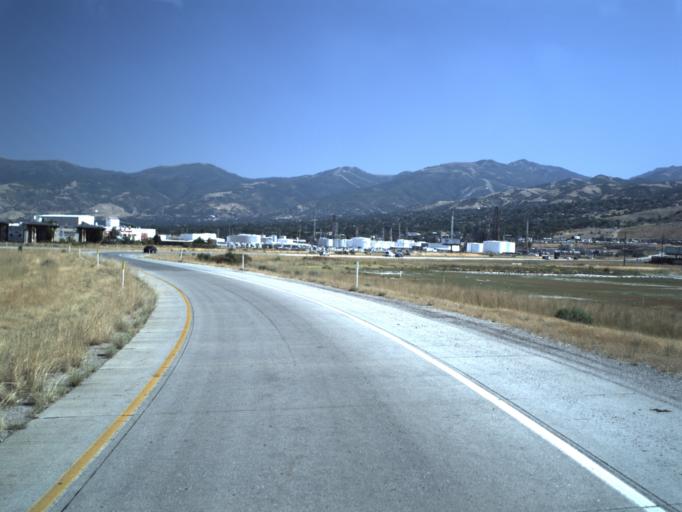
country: US
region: Utah
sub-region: Davis County
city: North Salt Lake
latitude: 40.8325
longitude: -111.9370
